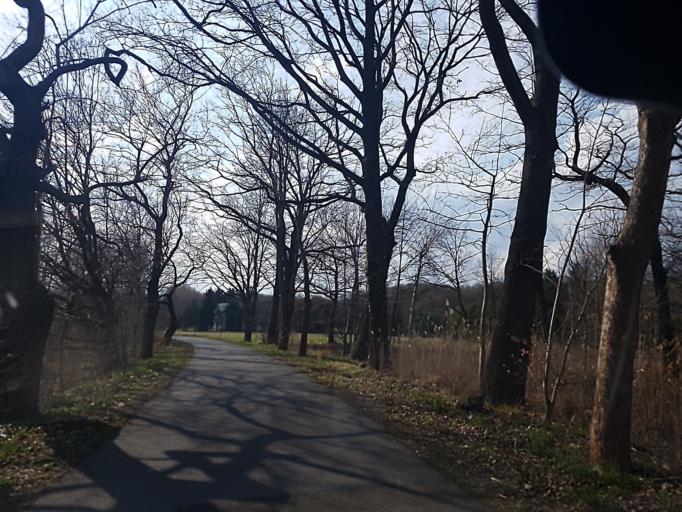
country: DE
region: Brandenburg
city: Doberlug-Kirchhain
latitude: 51.6108
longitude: 13.5413
